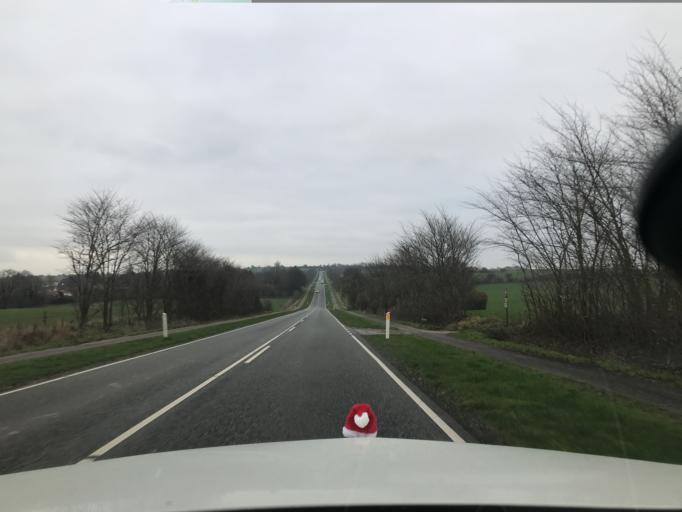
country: DK
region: South Denmark
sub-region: Sonderborg Kommune
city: Dybbol
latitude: 54.9088
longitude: 9.7269
